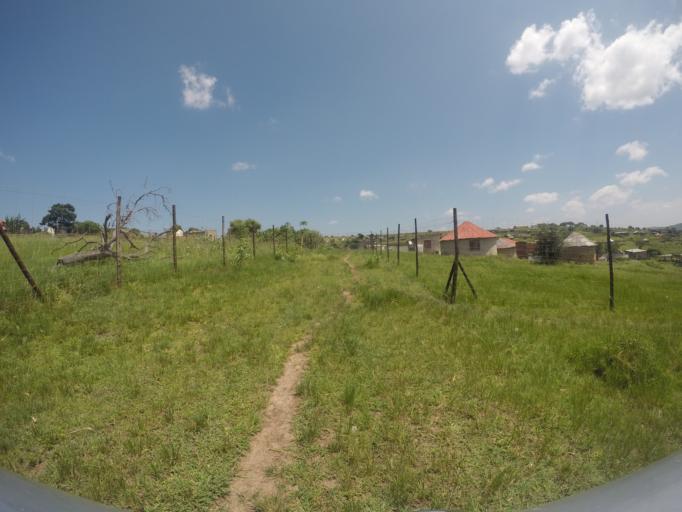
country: ZA
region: KwaZulu-Natal
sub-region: uThungulu District Municipality
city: Empangeni
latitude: -28.6059
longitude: 31.7388
